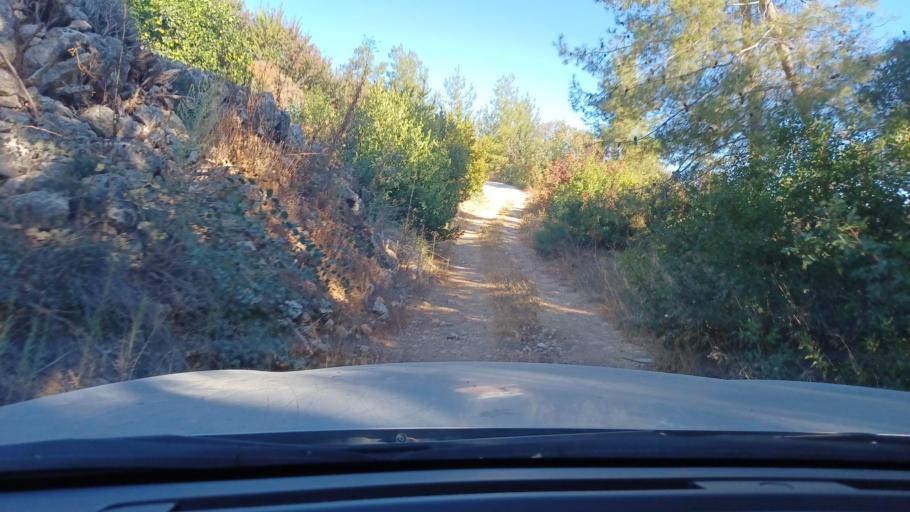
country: CY
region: Pafos
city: Polis
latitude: 34.9983
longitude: 32.5227
